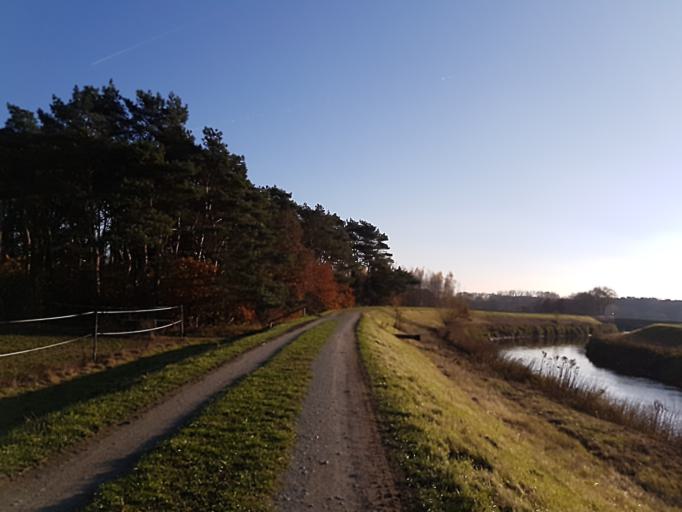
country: BE
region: Flanders
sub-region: Provincie Vlaams-Brabant
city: Boortmeerbeek
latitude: 50.9945
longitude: 4.6013
